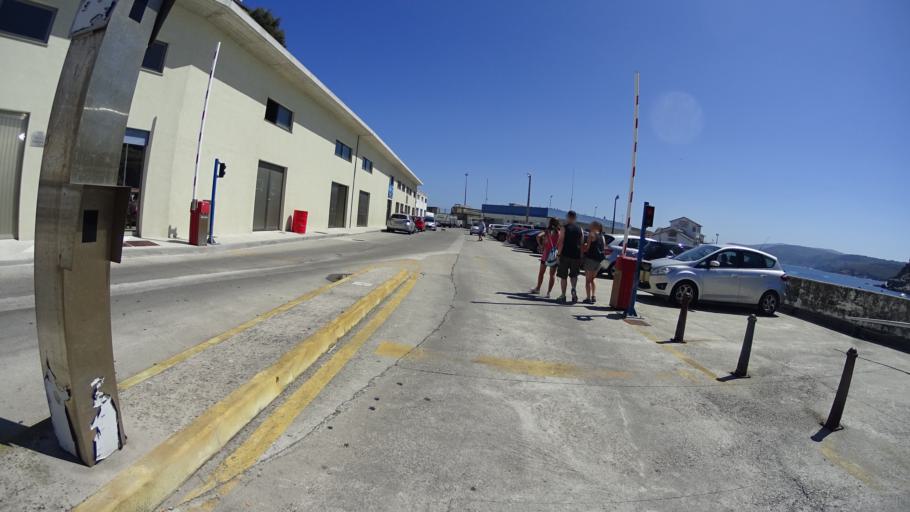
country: ES
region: Galicia
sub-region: Provincia da Coruna
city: Malpica
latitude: 43.3237
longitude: -8.8081
